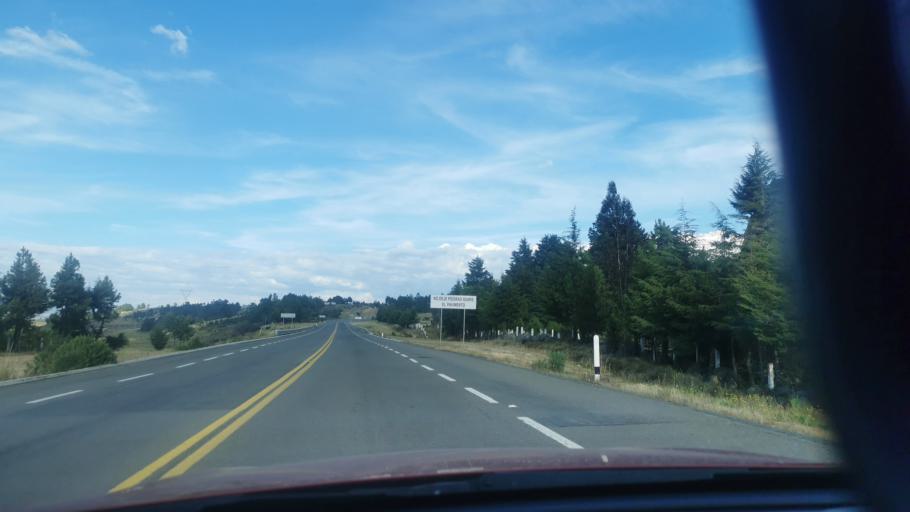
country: MX
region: Mexico
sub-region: Villa Victoria
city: Colonia Doctor Gustavo Baz
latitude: 19.3588
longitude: -99.9569
